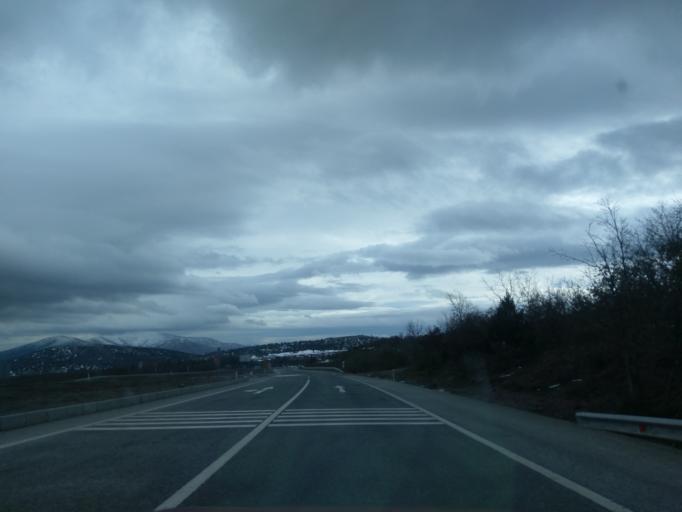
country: TR
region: Kuetahya
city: Aslanapa
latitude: 39.2753
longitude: 29.9173
